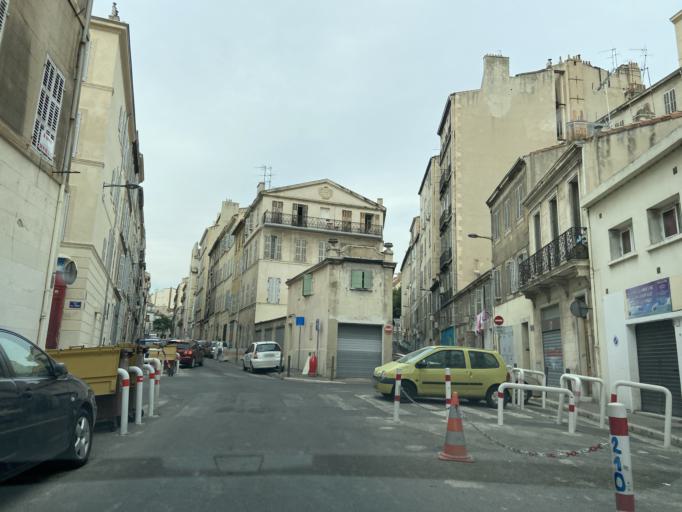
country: FR
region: Provence-Alpes-Cote d'Azur
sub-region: Departement des Bouches-du-Rhone
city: Marseille 04
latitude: 43.3019
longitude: 5.3928
